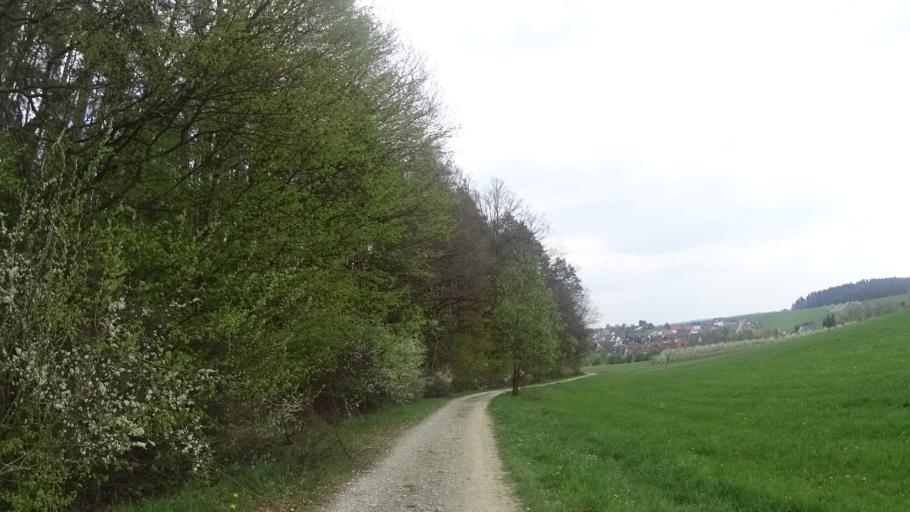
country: DE
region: Bavaria
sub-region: Upper Franconia
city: Igensdorf
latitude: 49.6209
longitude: 11.2174
